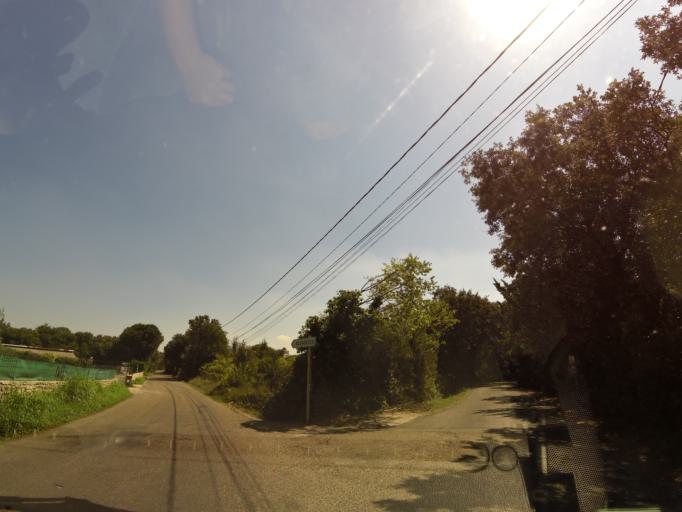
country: FR
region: Languedoc-Roussillon
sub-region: Departement du Gard
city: Villevieille
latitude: 43.8017
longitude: 4.1081
